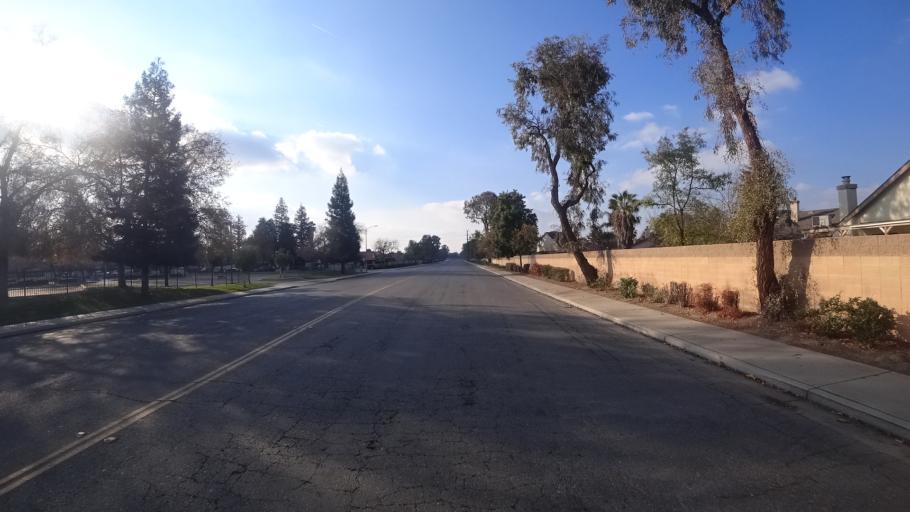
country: US
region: California
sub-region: Kern County
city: Greenacres
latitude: 35.3132
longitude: -119.0930
